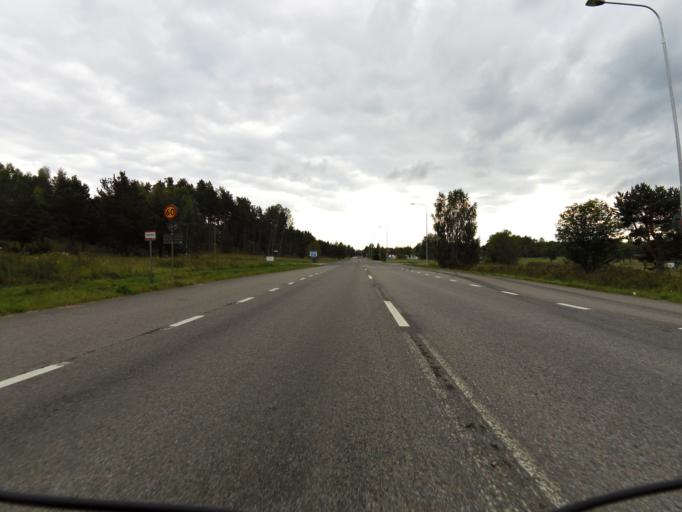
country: SE
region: Gaevleborg
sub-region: Sandvikens Kommun
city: Sandviken
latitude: 60.6461
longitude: 16.7948
